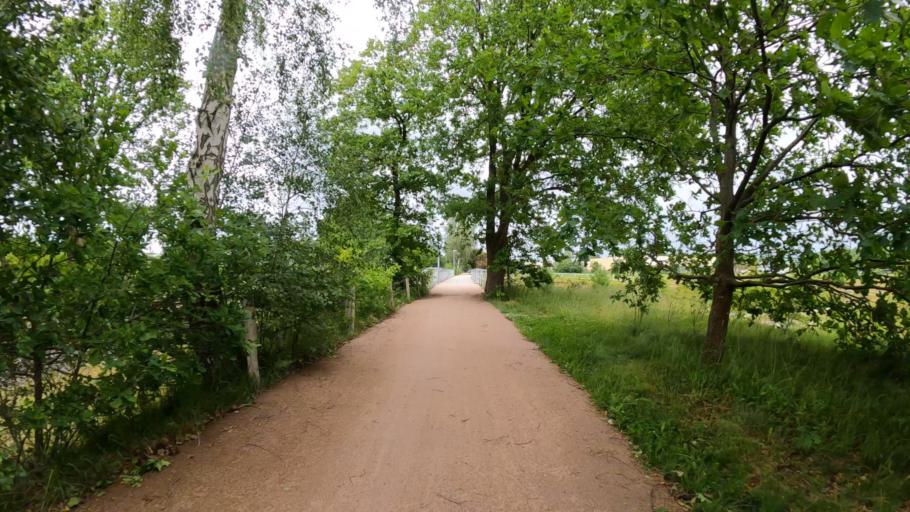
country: DE
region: Schleswig-Holstein
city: Norderstedt
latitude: 53.7215
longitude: 9.9911
